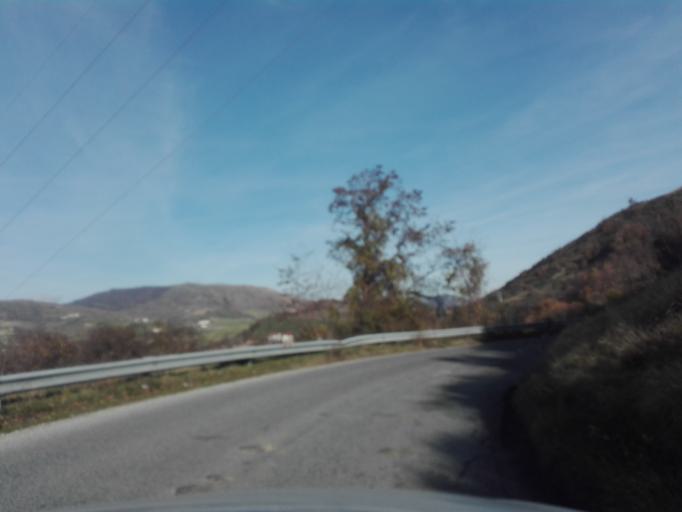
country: IT
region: Molise
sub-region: Provincia di Isernia
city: Agnone
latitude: 41.8212
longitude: 14.3741
